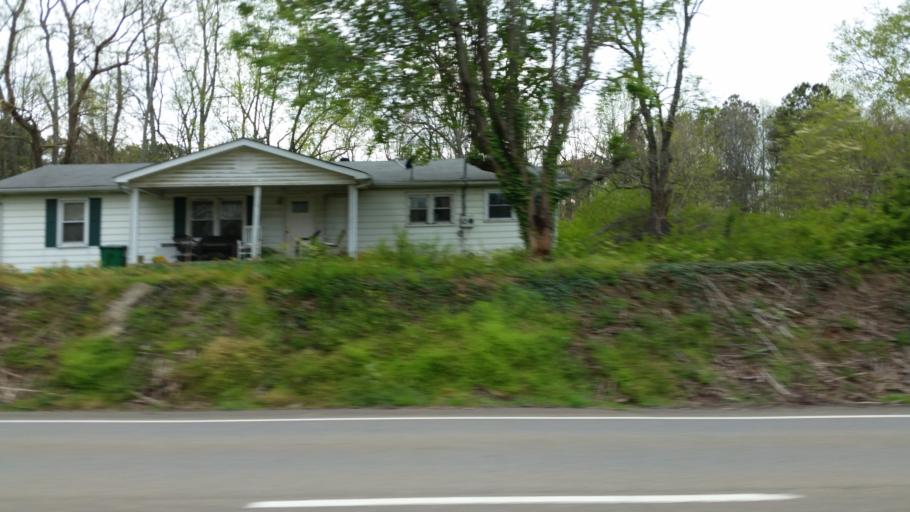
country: US
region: Georgia
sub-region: Pickens County
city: Jasper
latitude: 34.4951
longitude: -84.4695
